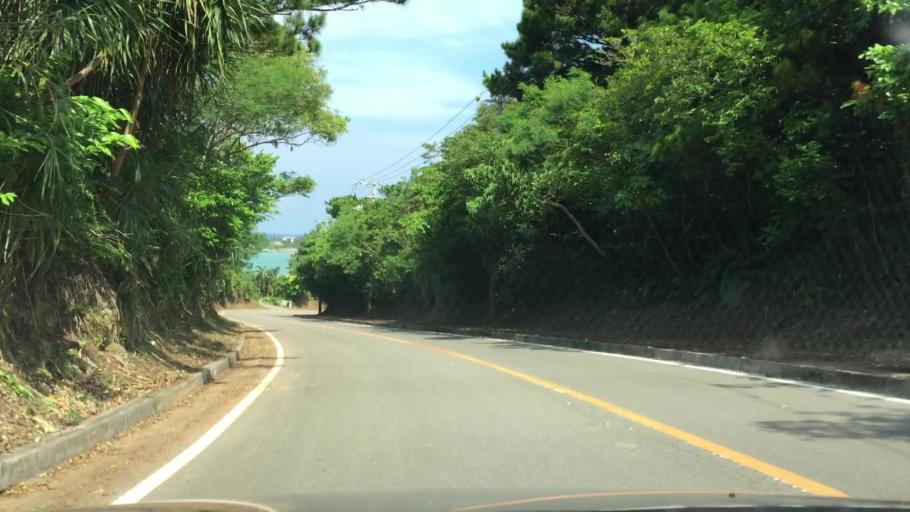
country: JP
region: Okinawa
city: Ishigaki
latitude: 24.5097
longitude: 124.2684
